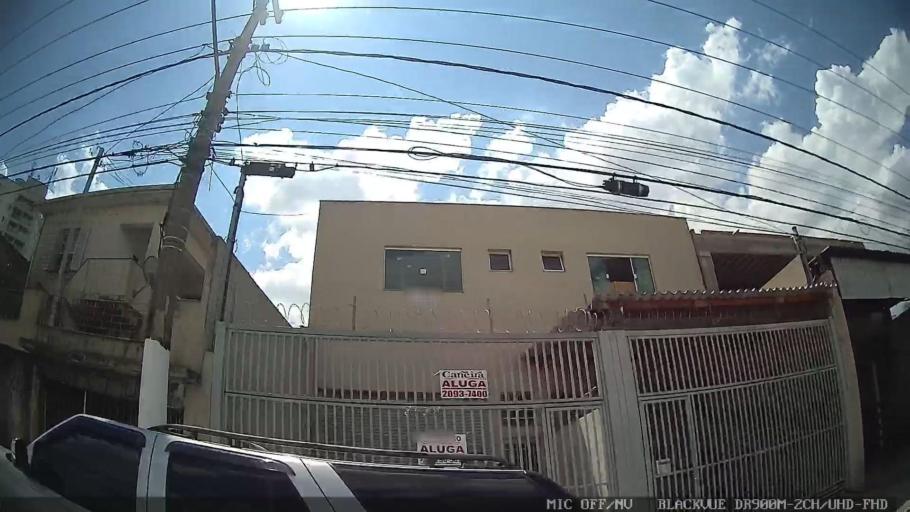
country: BR
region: Sao Paulo
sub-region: Ferraz De Vasconcelos
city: Ferraz de Vasconcelos
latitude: -23.5530
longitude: -46.4654
